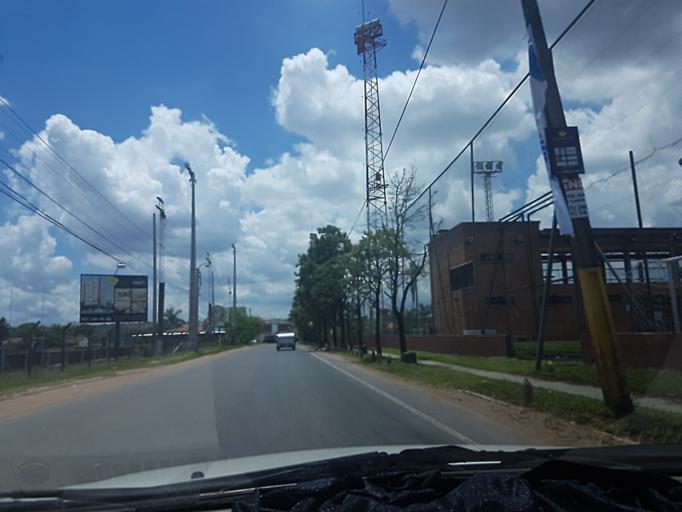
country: PY
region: Central
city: Fernando de la Mora
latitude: -25.2864
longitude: -57.5442
